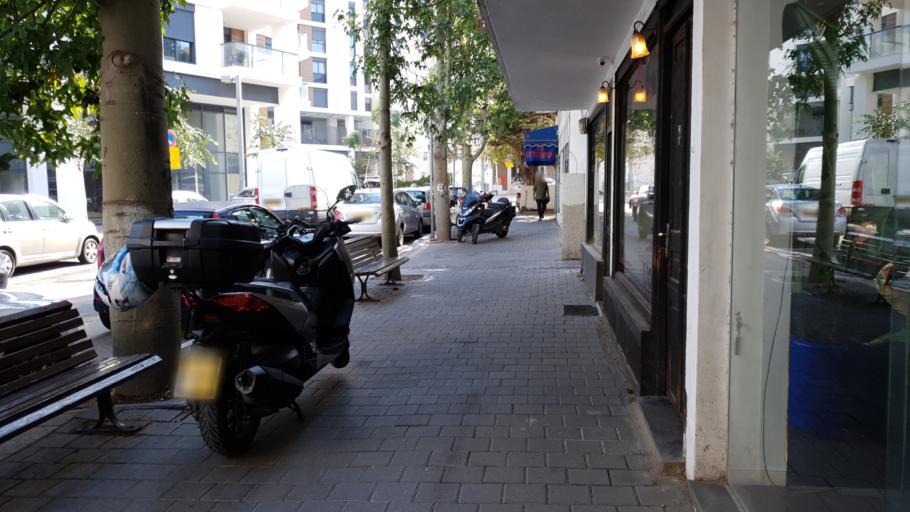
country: IL
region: Tel Aviv
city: Tel Aviv
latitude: 32.0718
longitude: 34.7712
